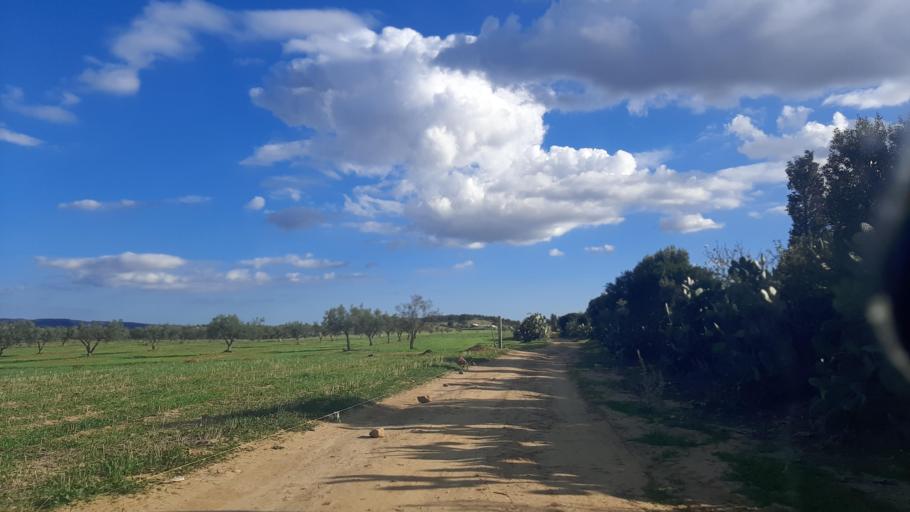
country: TN
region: Nabul
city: Bu `Urqub
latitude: 36.4642
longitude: 10.4838
